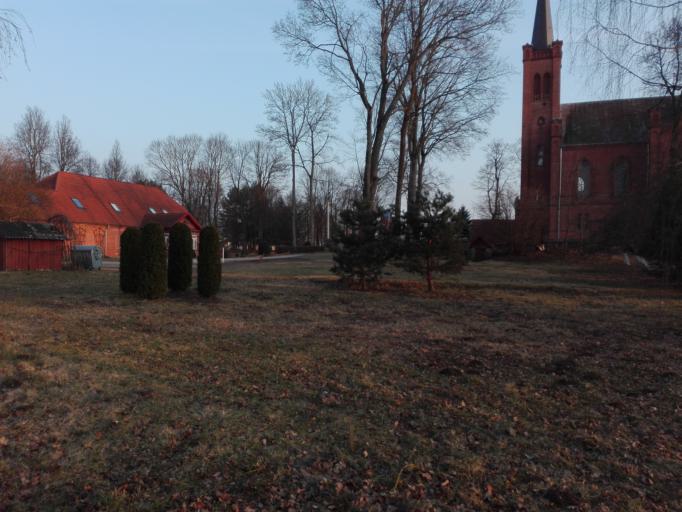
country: LT
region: Panevezys
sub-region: Birzai
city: Birzai
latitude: 56.2087
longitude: 24.7584
